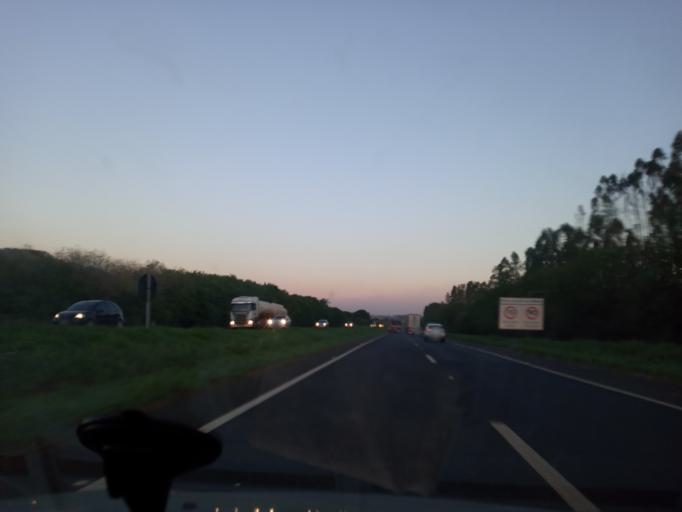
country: BR
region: Minas Gerais
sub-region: Uberlandia
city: Uberlandia
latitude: -18.8819
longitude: -48.4847
